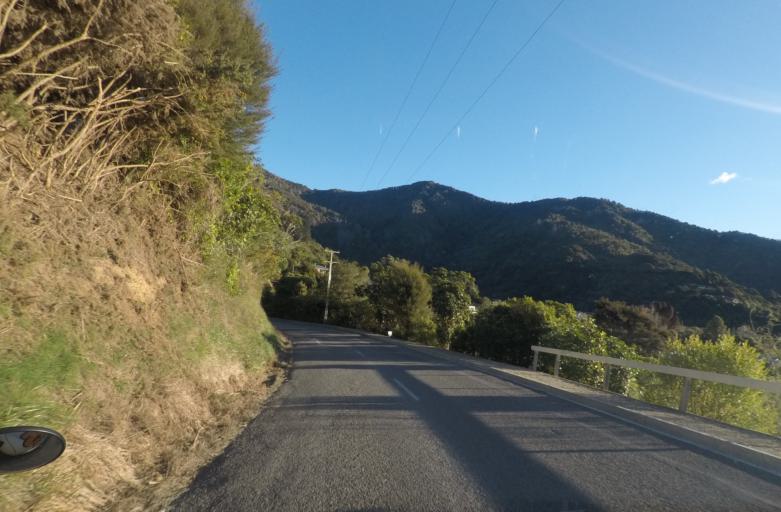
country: NZ
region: Marlborough
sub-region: Marlborough District
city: Picton
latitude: -41.2744
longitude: 173.9668
